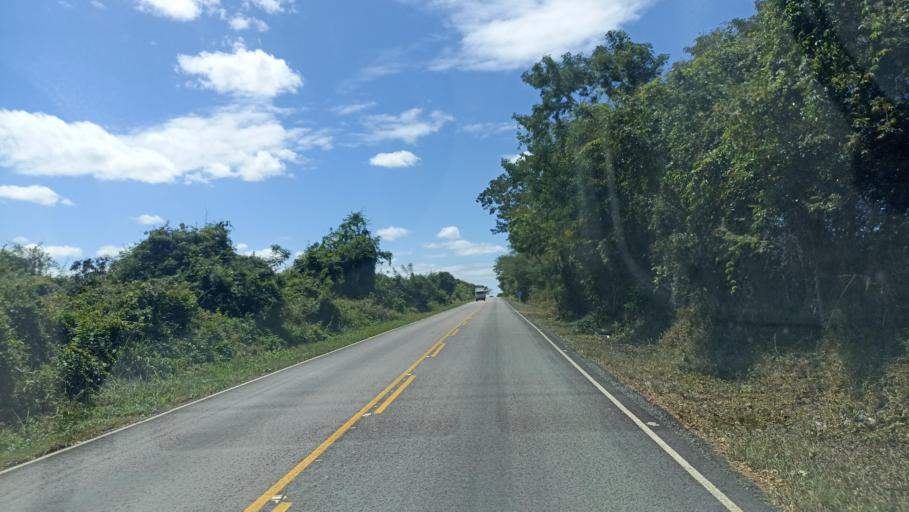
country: BR
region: Bahia
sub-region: Andarai
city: Vera Cruz
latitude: -12.7501
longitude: -41.3269
